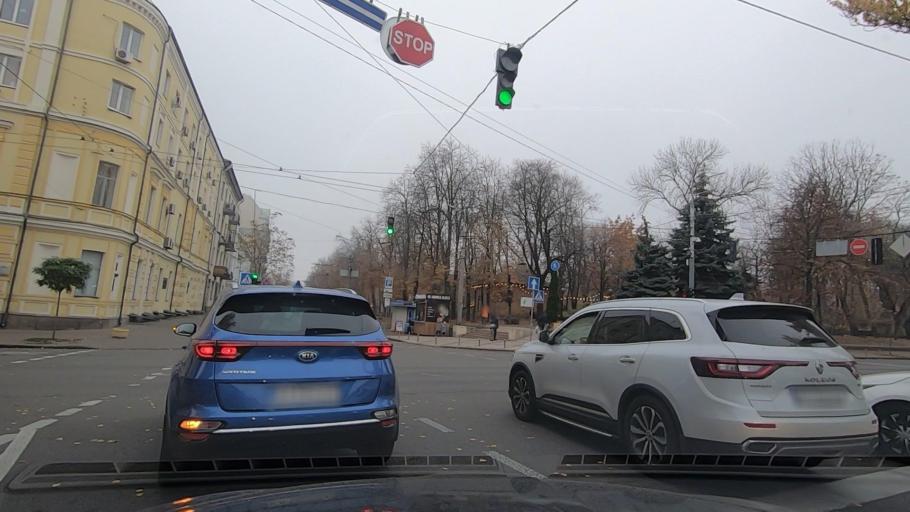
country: BY
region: Gomel
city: Narowlya
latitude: 51.7780
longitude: 29.4251
